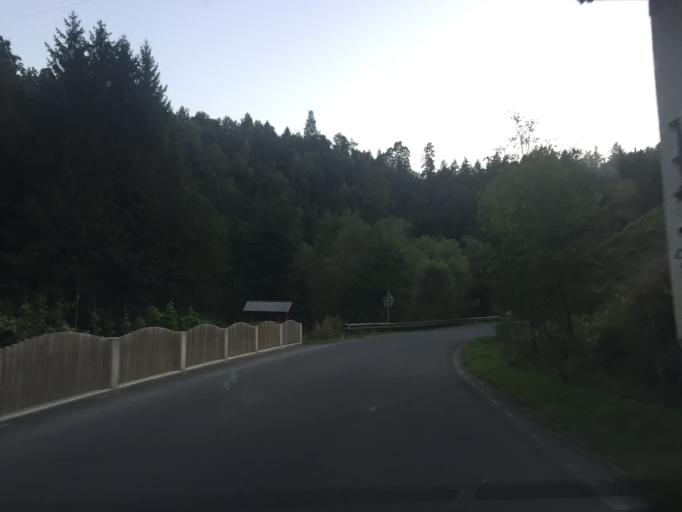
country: SI
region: Sostanj
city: Topolsica
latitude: 46.3770
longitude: 15.0249
